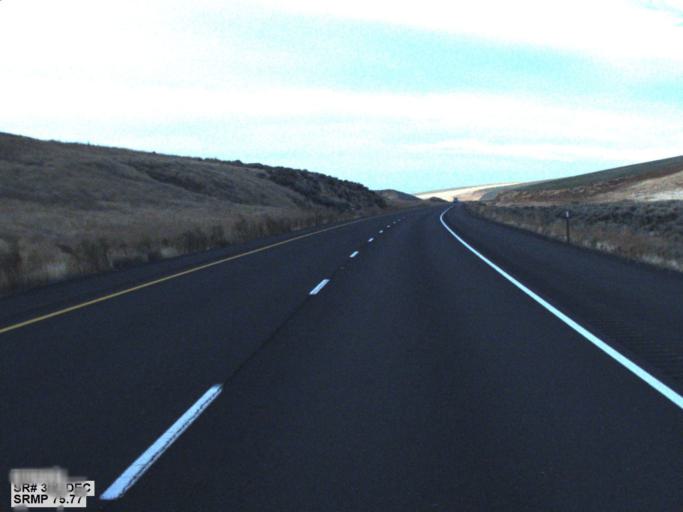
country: US
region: Washington
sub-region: Franklin County
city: Connell
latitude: 46.8854
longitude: -118.6187
